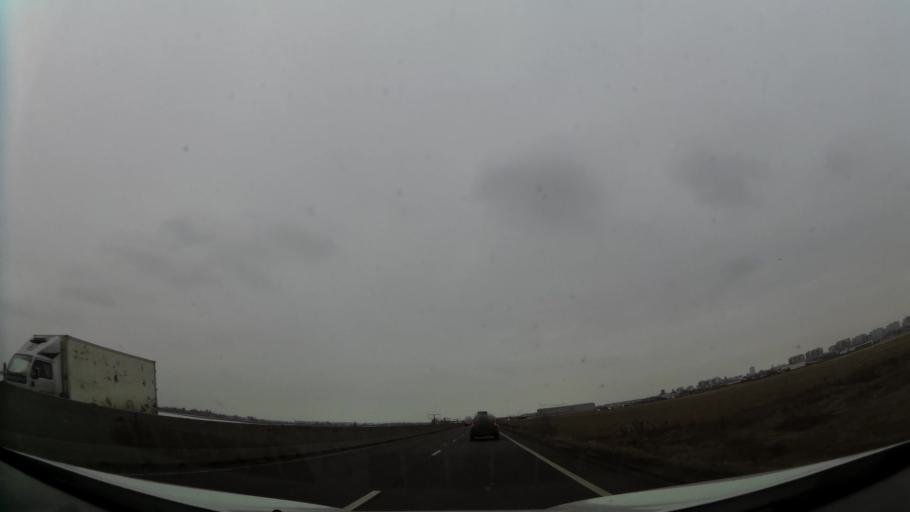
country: RO
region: Prahova
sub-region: Comuna Targsoru Vechi
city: Strejnicu
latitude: 44.9182
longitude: 25.9868
